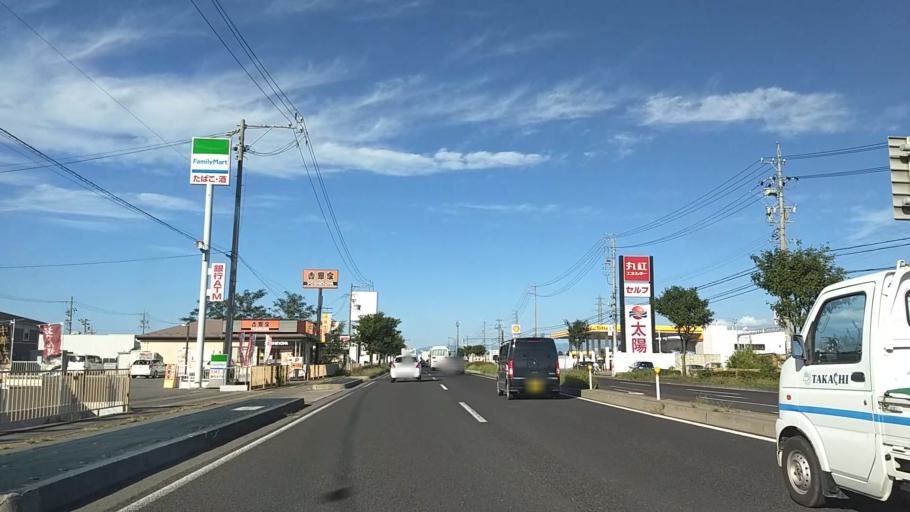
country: JP
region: Nagano
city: Nagano-shi
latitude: 36.5770
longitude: 138.1578
